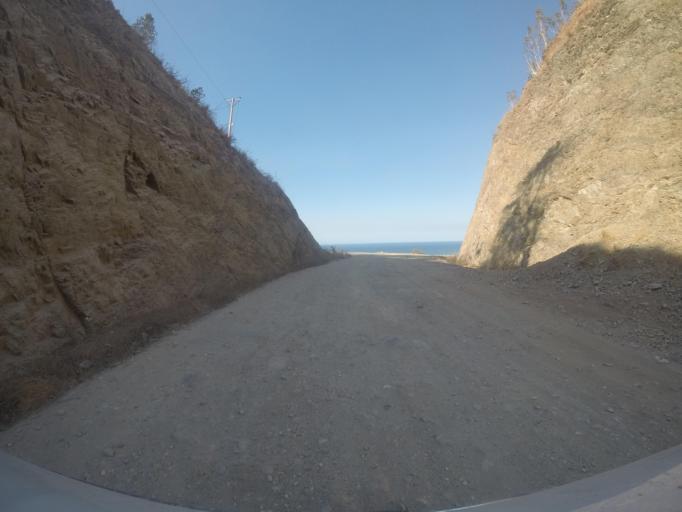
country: TL
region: Dili
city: Dili
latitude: -8.5300
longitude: 125.6203
